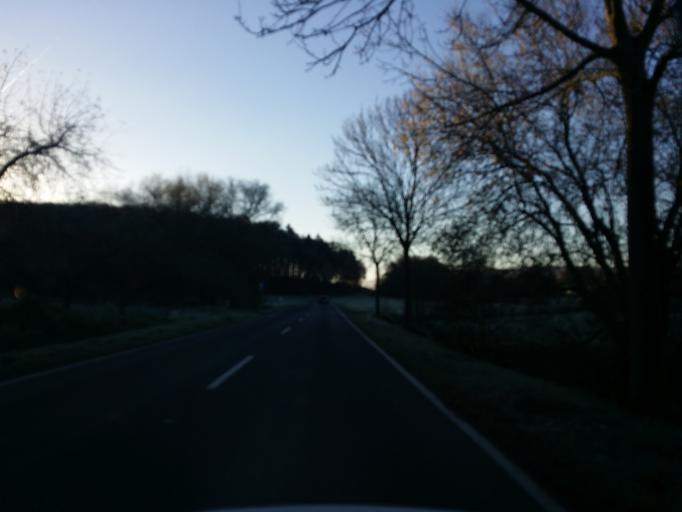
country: DE
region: Hesse
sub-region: Regierungsbezirk Darmstadt
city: Waldems
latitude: 50.2440
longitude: 8.3234
